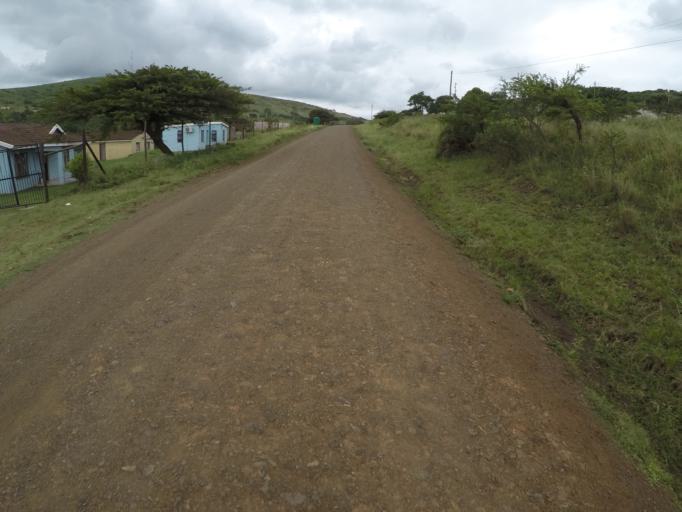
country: ZA
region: KwaZulu-Natal
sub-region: uThungulu District Municipality
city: Empangeni
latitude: -28.7071
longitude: 31.8484
